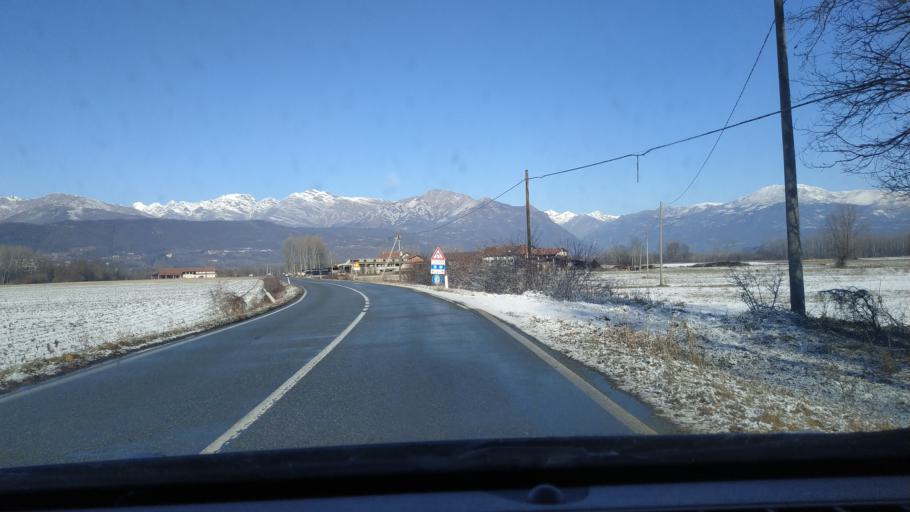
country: IT
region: Piedmont
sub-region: Provincia di Torino
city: Perosa Canavese
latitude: 45.4052
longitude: 7.8299
